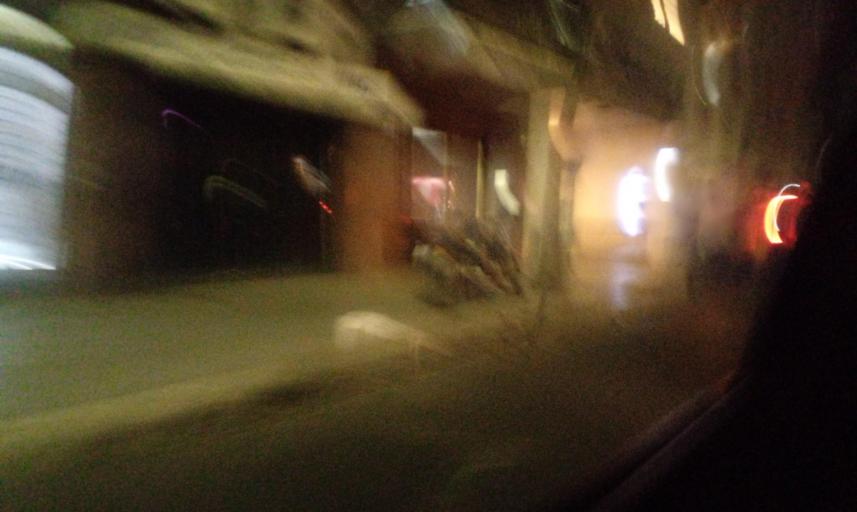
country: AR
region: Buenos Aires F.D.
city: Villa Santa Rita
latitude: -34.6180
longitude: -58.4381
